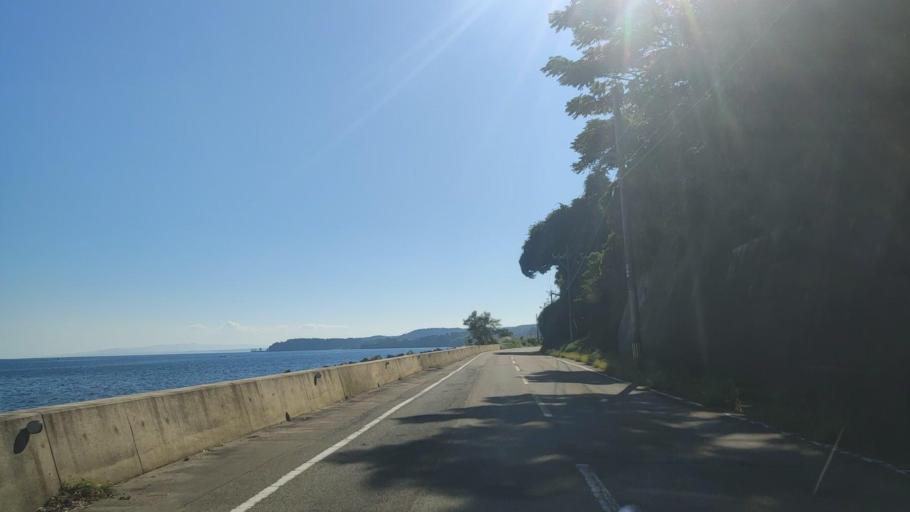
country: JP
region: Ishikawa
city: Nanao
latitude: 37.2816
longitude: 137.1080
